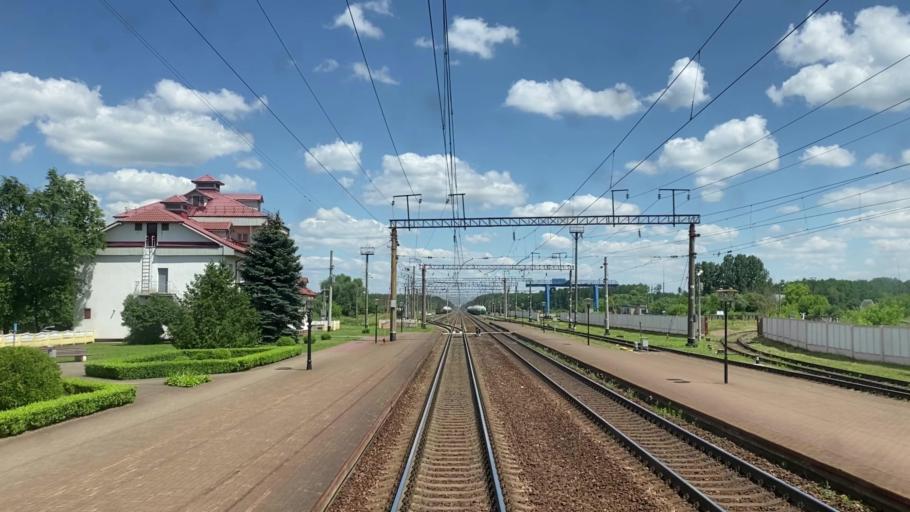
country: BY
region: Brest
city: Pruzhany
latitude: 52.4706
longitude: 24.5235
